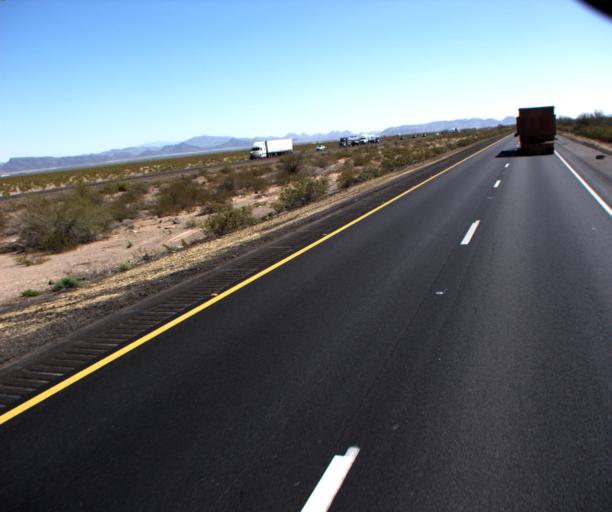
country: US
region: Arizona
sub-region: La Paz County
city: Salome
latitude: 33.6382
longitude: -113.8187
